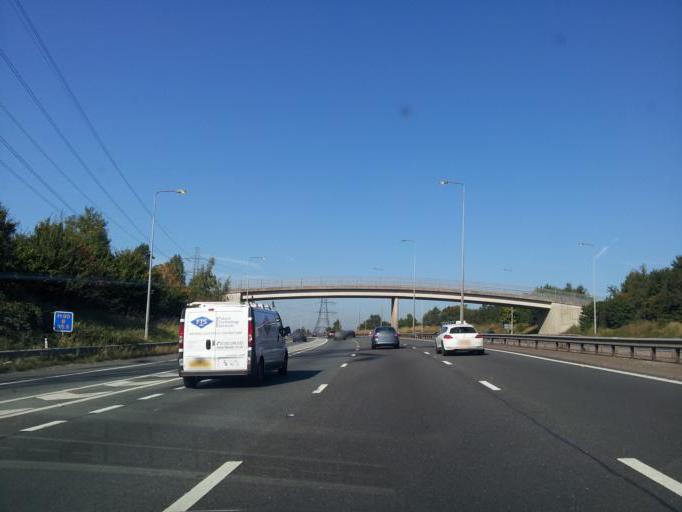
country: GB
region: England
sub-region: Borough of Rochdale
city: Middleton
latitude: 53.5376
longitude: -2.2109
